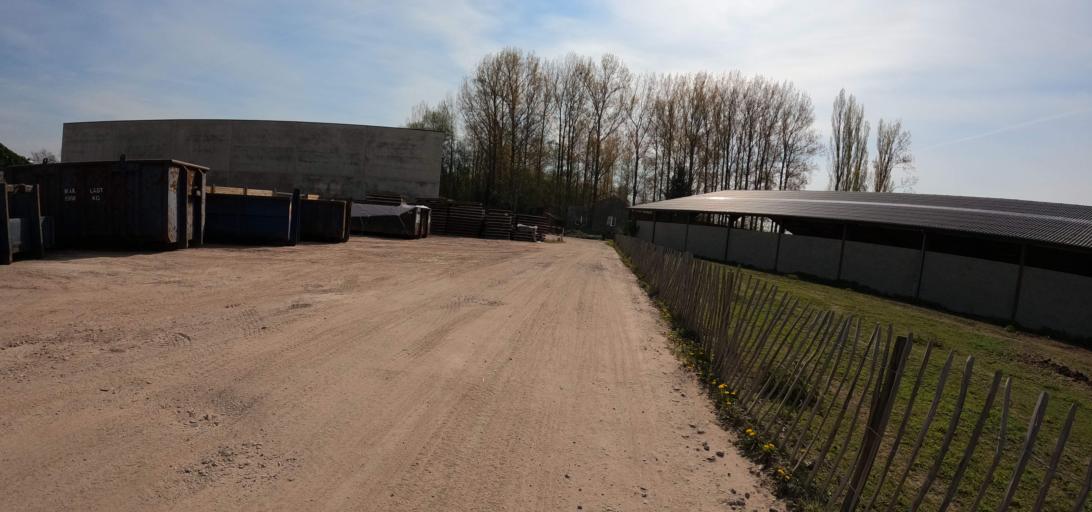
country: BE
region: Flanders
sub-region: Provincie Antwerpen
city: Ranst
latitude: 51.2043
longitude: 4.5813
